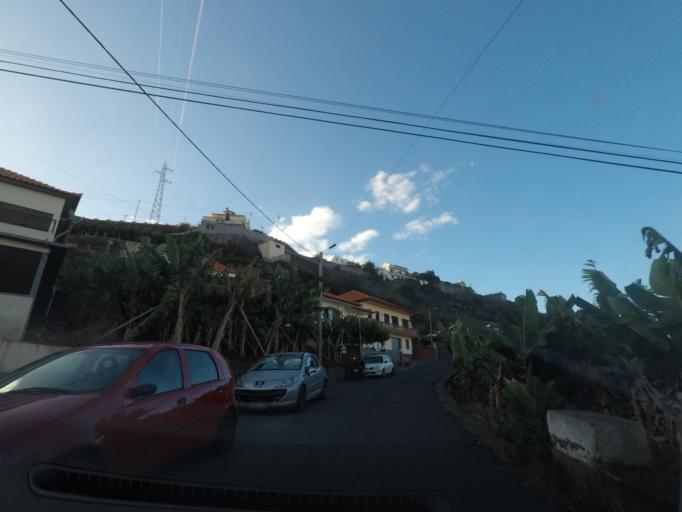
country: PT
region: Madeira
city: Ponta do Sol
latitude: 32.6866
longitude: -17.0924
